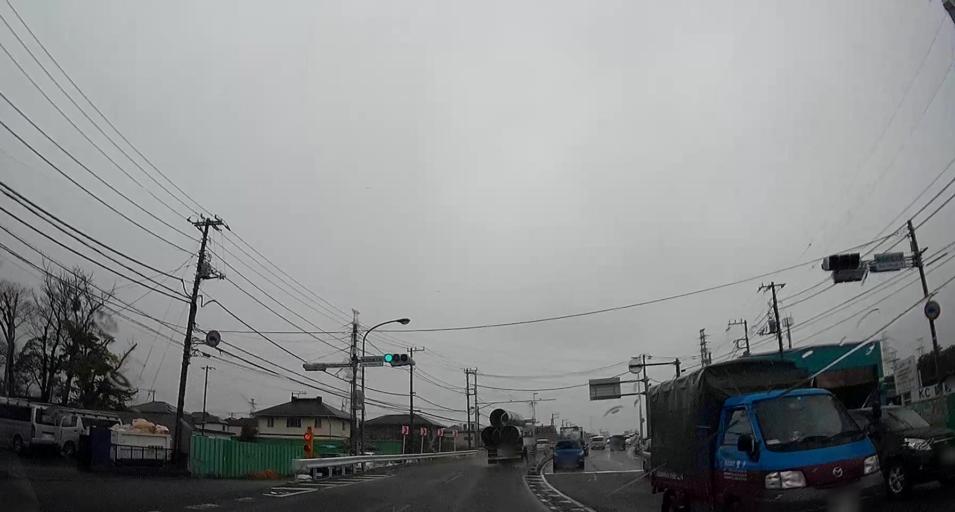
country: JP
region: Chiba
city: Chiba
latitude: 35.5683
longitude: 140.1298
